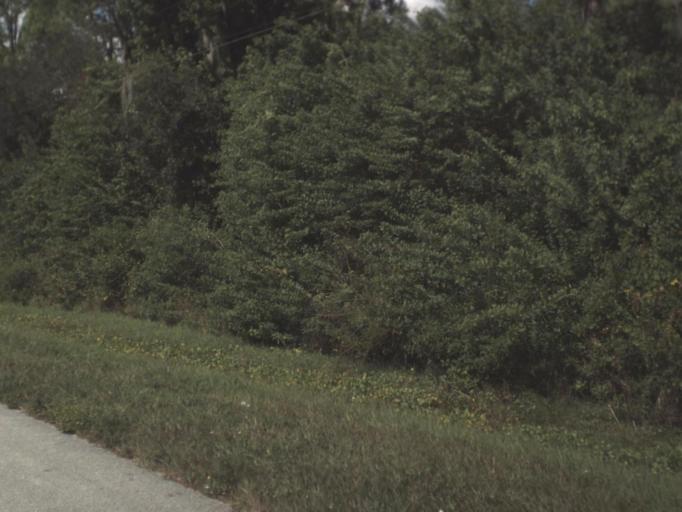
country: US
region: Florida
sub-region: Highlands County
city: Sebring
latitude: 27.4125
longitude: -81.4769
